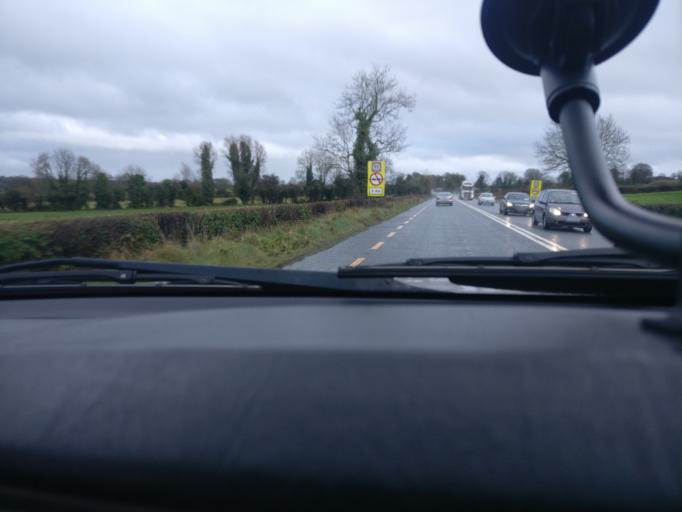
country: IE
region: Leinster
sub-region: An Mhi
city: Enfield
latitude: 53.4212
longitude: -6.7577
